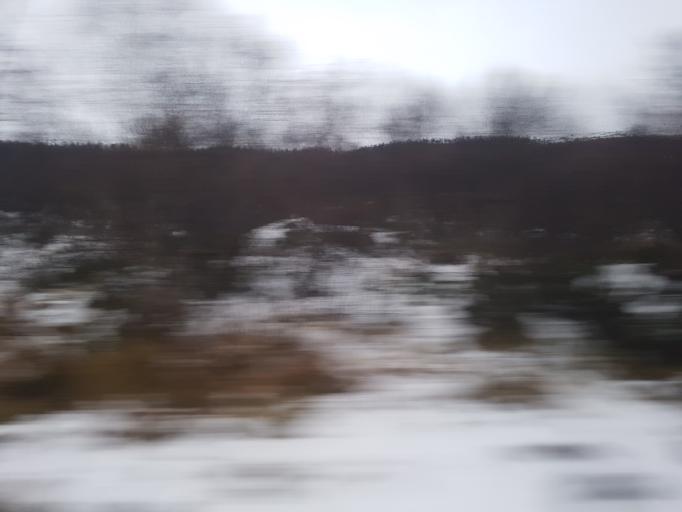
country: NO
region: Sor-Trondelag
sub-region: Oppdal
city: Oppdal
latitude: 62.3054
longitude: 9.6058
